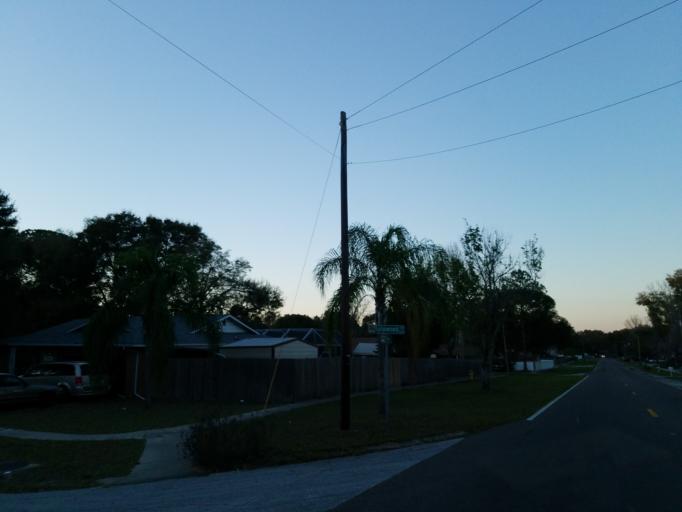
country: US
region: Florida
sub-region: Hillsborough County
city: Mango
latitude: 27.9851
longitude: -82.2941
